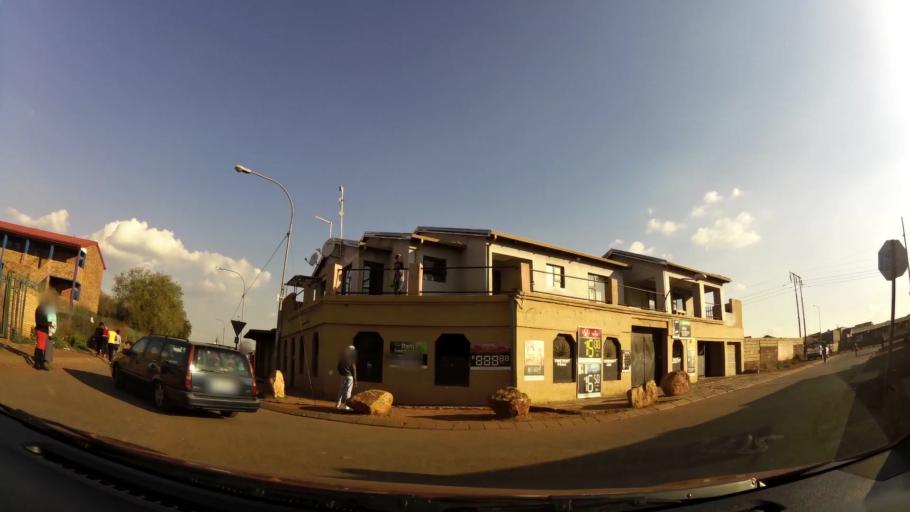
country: ZA
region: Gauteng
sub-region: City of Johannesburg Metropolitan Municipality
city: Soweto
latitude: -26.2278
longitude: 27.8590
